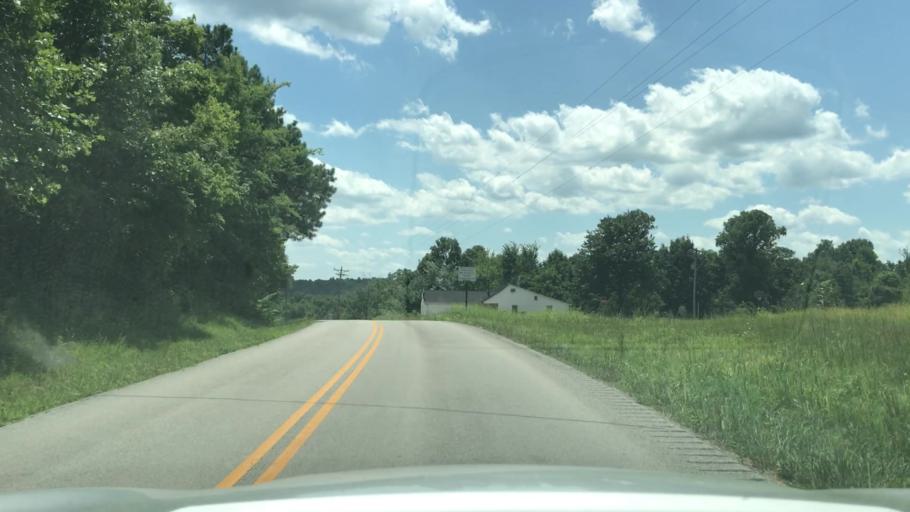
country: US
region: Kentucky
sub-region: Hopkins County
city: Nortonville
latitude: 37.1021
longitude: -87.3399
